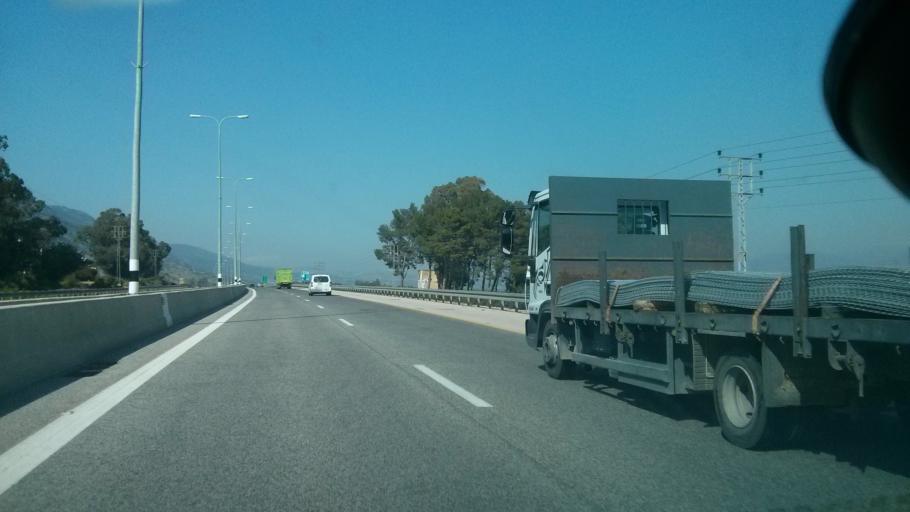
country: IL
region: Northern District
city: Qiryat Shemona
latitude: 33.1177
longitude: 35.5719
